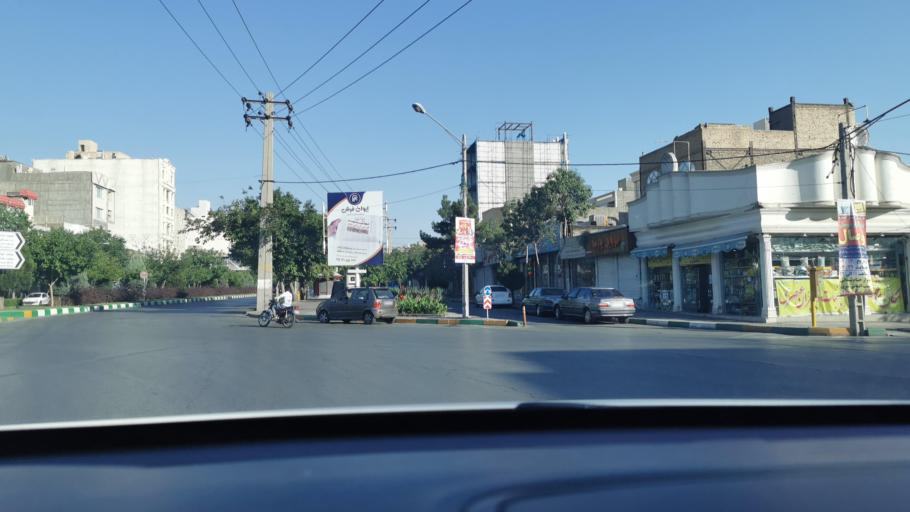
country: IR
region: Razavi Khorasan
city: Mashhad
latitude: 36.2961
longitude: 59.5295
